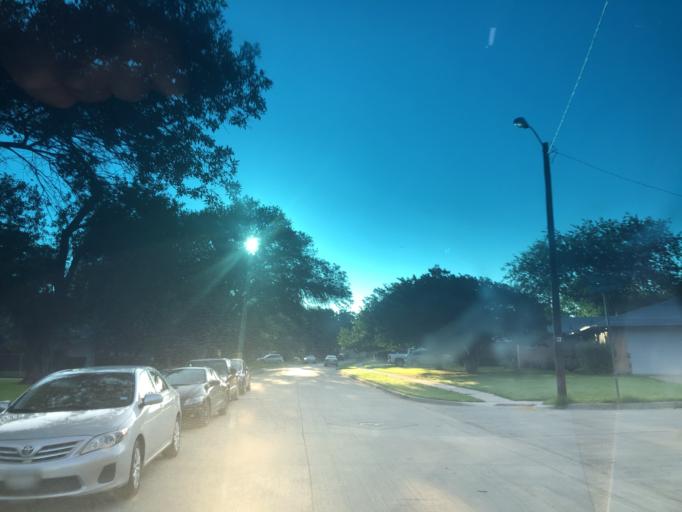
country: US
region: Texas
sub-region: Dallas County
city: Grand Prairie
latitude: 32.7043
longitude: -97.0131
